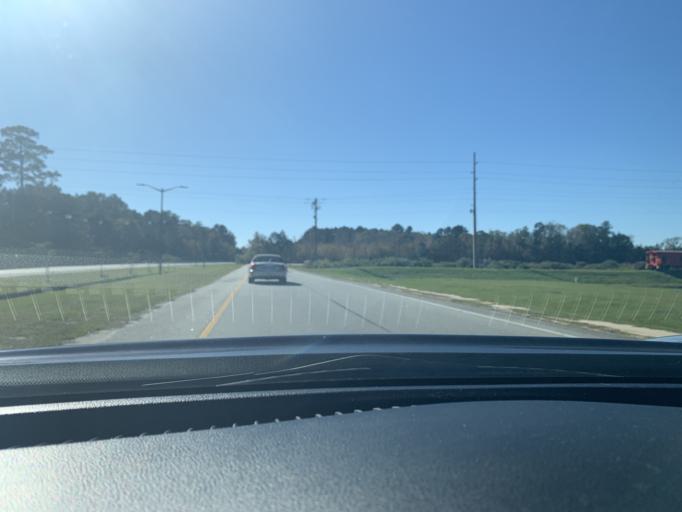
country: US
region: Georgia
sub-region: Chatham County
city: Pooler
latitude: 32.1206
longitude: -81.2662
